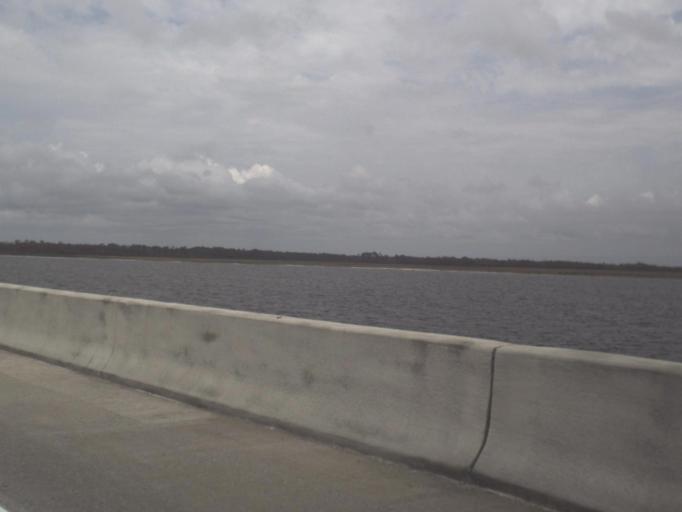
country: US
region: Florida
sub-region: Santa Rosa County
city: Oriole Beach
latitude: 30.4336
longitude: -87.0975
